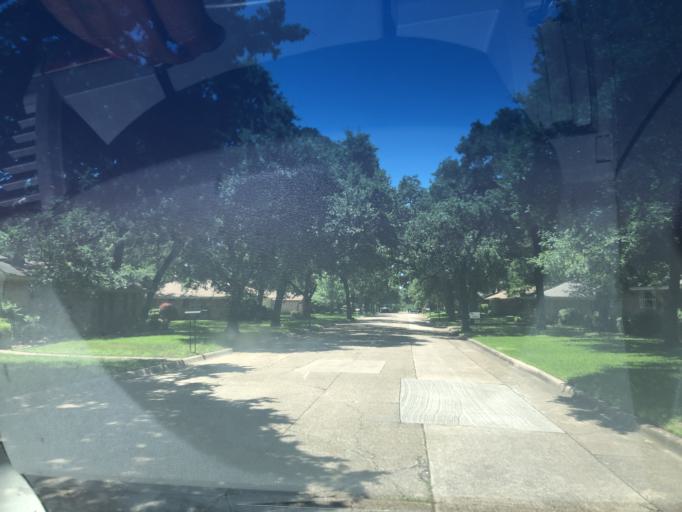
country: US
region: Texas
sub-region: Dallas County
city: Grand Prairie
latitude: 32.7789
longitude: -97.0357
